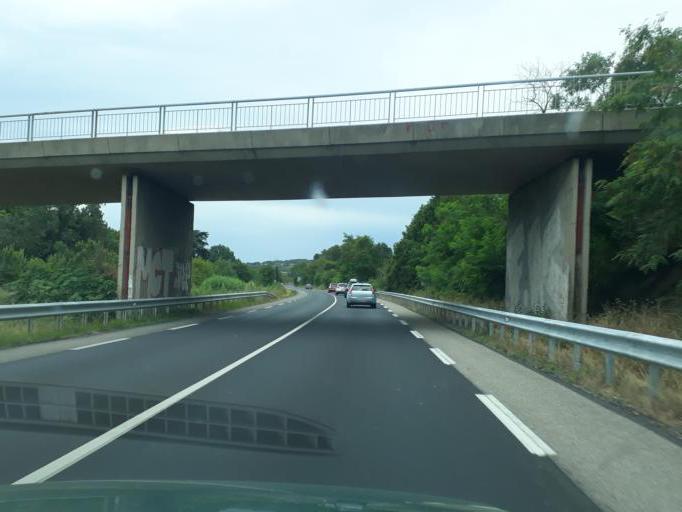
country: FR
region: Languedoc-Roussillon
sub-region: Departement de l'Herault
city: Saint-Thibery
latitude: 43.4028
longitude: 3.4103
